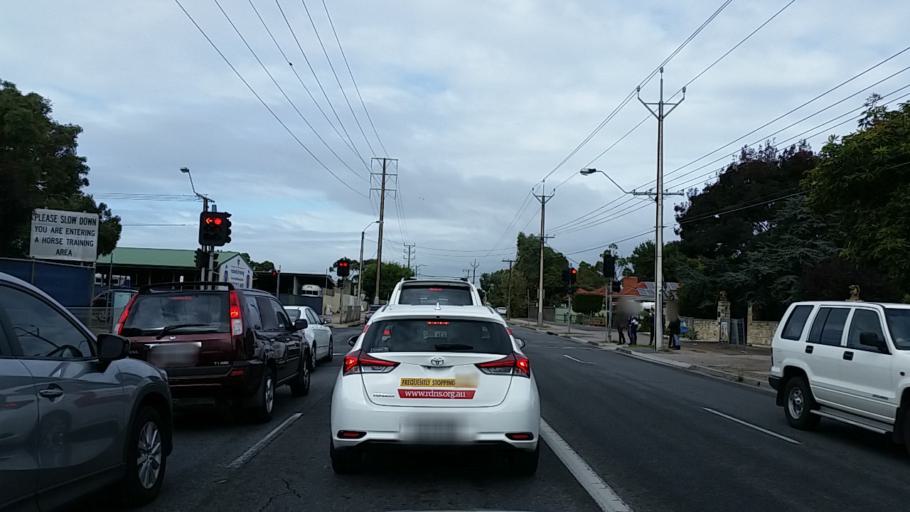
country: AU
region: South Australia
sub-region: Marion
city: Plympton Park
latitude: -34.9810
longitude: 138.5382
